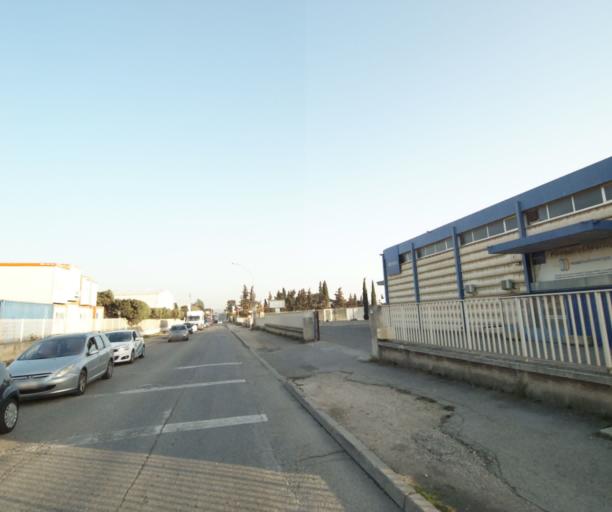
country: FR
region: Provence-Alpes-Cote d'Azur
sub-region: Departement des Bouches-du-Rhone
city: Vitrolles
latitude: 43.4395
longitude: 5.2430
